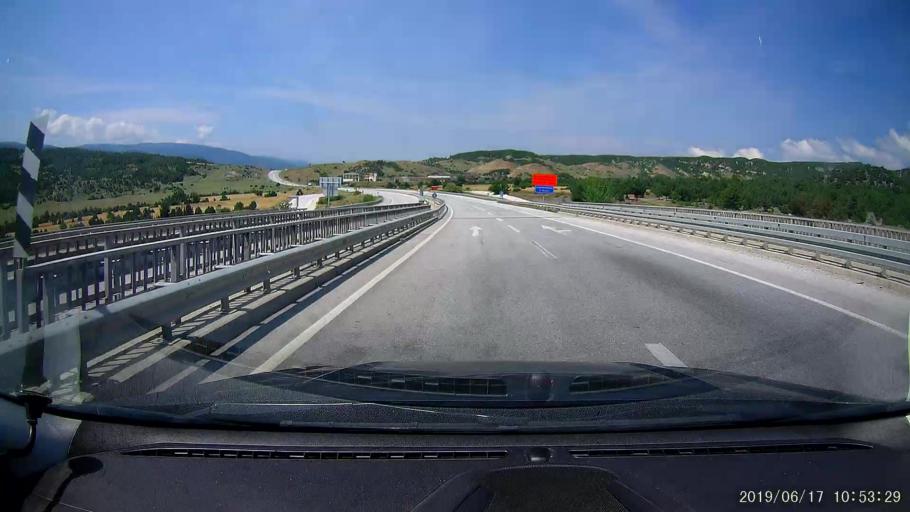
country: TR
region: Corum
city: Hacihamza
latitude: 41.0833
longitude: 34.3199
